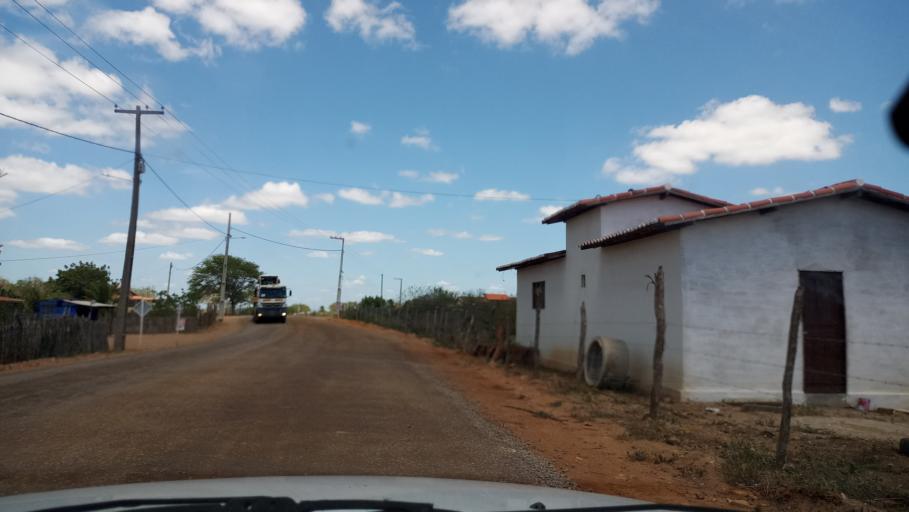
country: BR
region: Rio Grande do Norte
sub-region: Sao Paulo Do Potengi
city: Sao Paulo do Potengi
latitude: -5.7847
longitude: -35.9154
